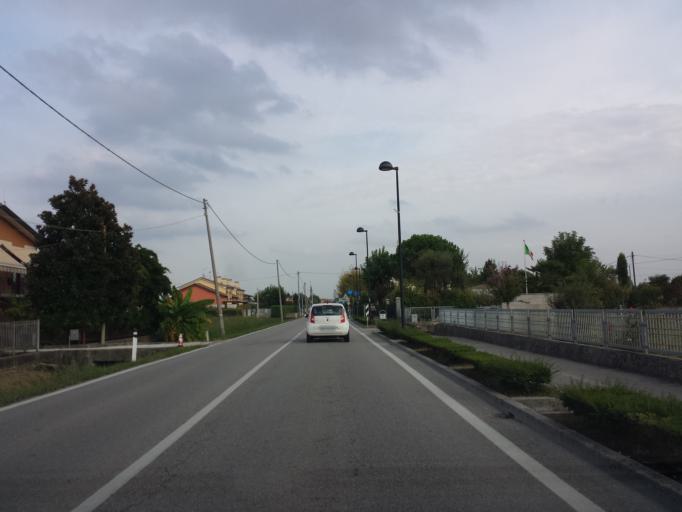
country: IT
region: Veneto
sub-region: Provincia di Padova
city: Campodarsego
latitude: 45.4980
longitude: 11.9282
